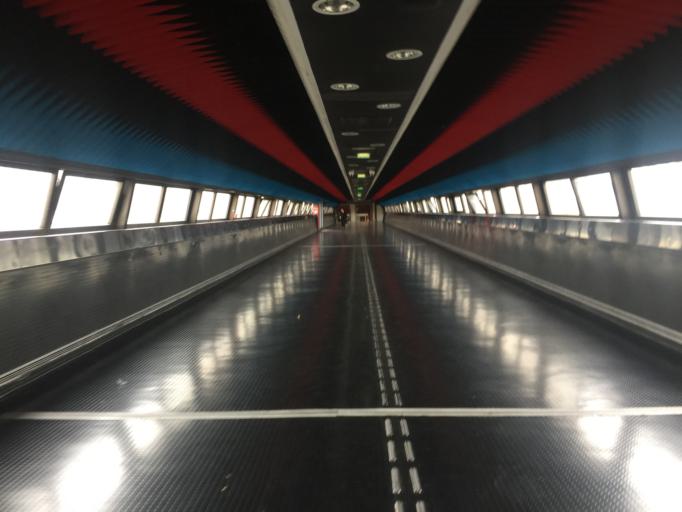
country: FR
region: Ile-de-France
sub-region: Departement des Yvelines
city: Montigny-le-Bretonneux
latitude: 48.7875
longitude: 2.0445
